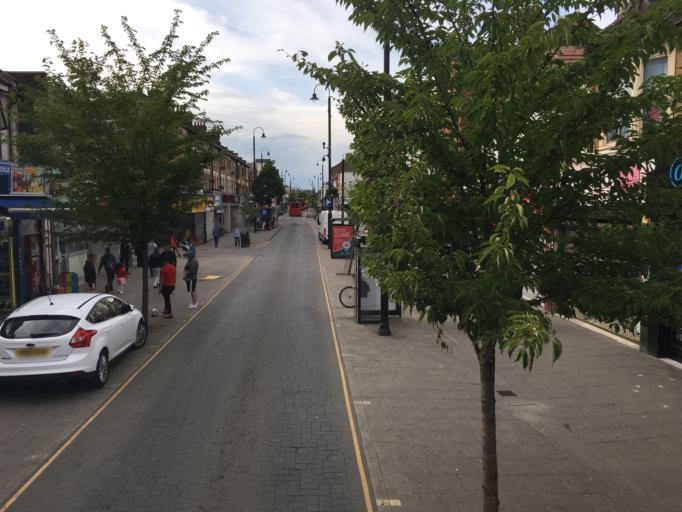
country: GB
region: England
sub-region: Greater London
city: East Ham
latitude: 51.5341
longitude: 0.0535
